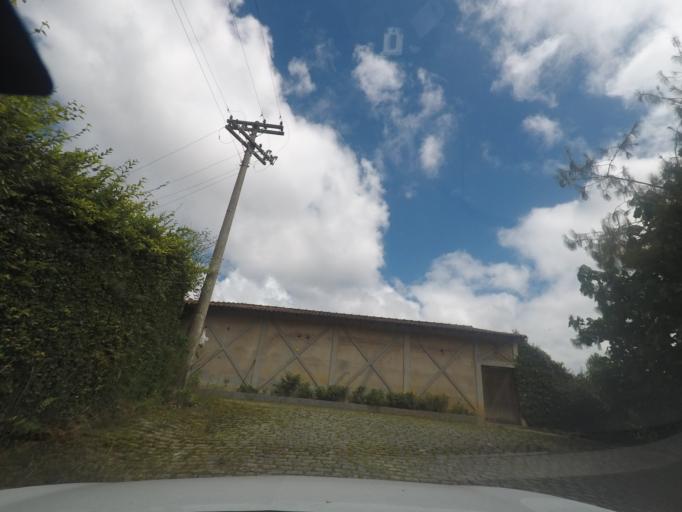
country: BR
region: Rio de Janeiro
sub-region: Teresopolis
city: Teresopolis
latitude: -22.3992
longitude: -42.9867
